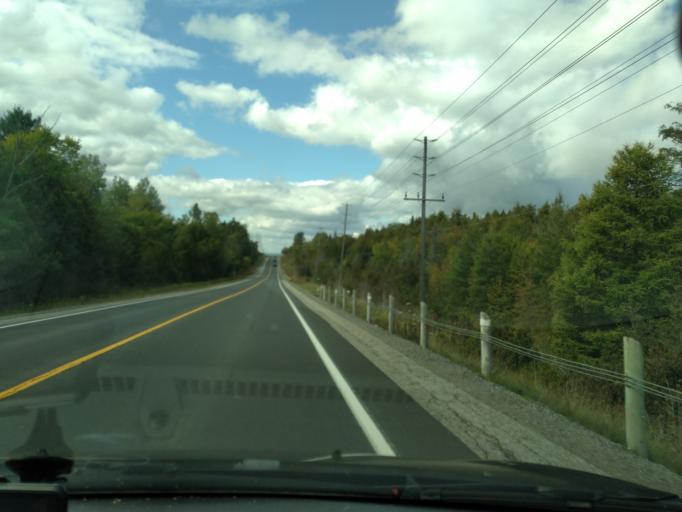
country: CA
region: Ontario
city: Innisfil
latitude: 44.2642
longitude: -79.7521
